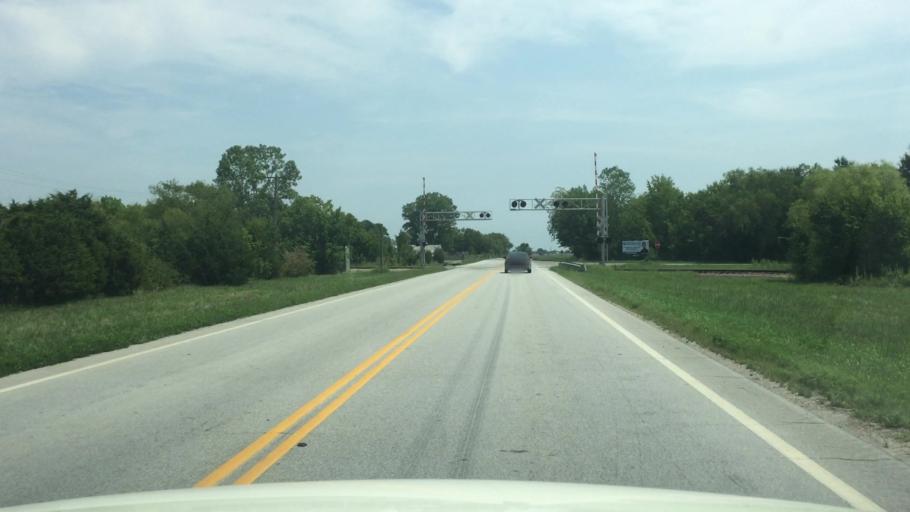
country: US
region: Kansas
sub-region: Cherokee County
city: Columbus
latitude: 37.1798
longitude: -94.9489
